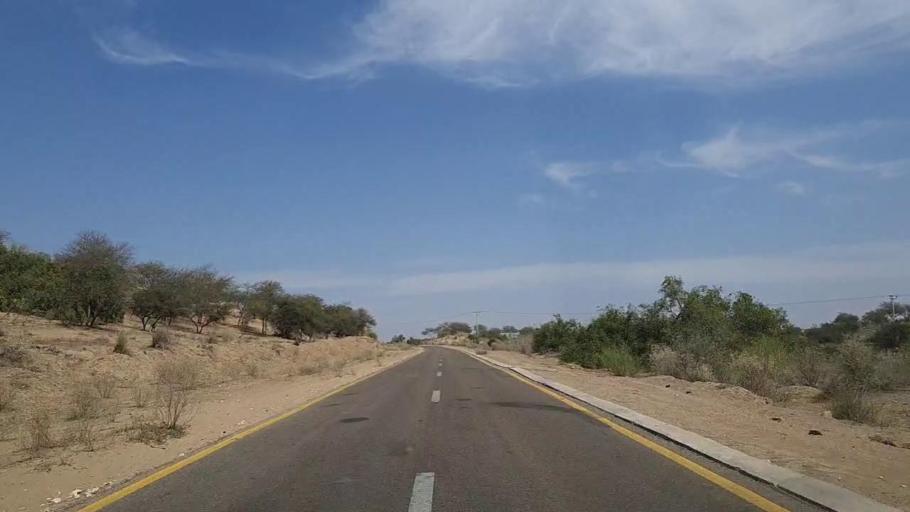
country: PK
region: Sindh
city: Mithi
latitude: 24.8311
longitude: 69.8301
